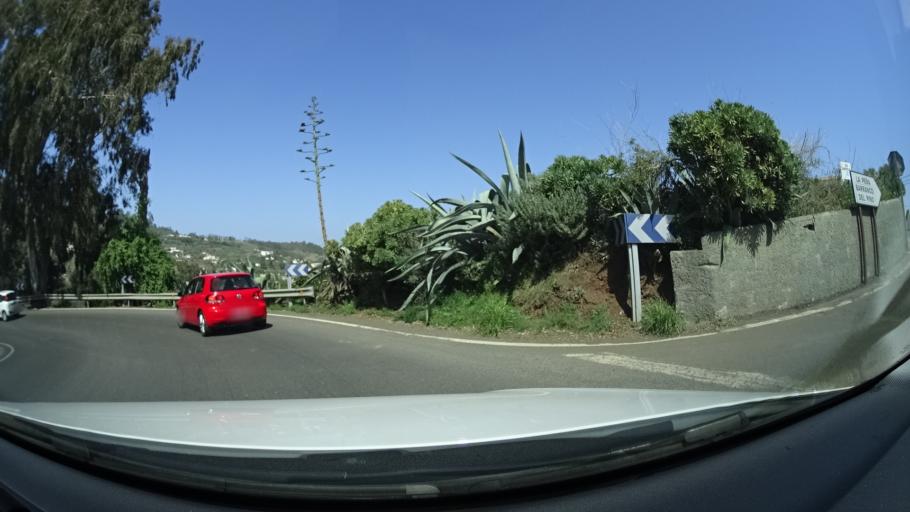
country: ES
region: Canary Islands
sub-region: Provincia de Las Palmas
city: Teror
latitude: 28.0758
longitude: -15.5382
